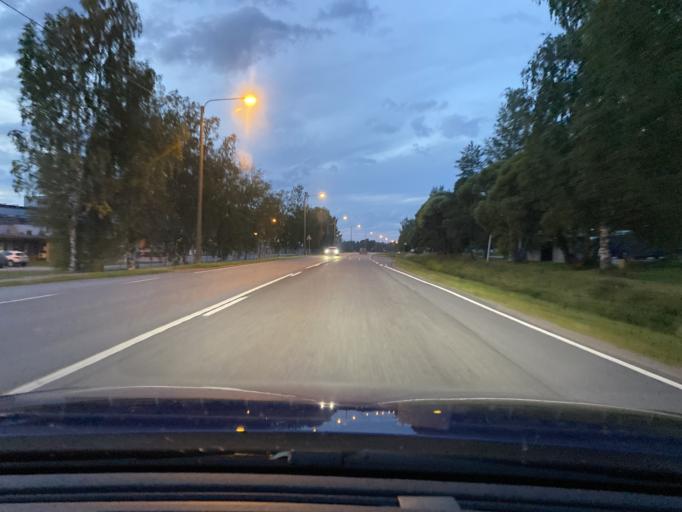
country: FI
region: Southern Ostrobothnia
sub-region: Suupohja
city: Kauhajoki
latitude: 62.4445
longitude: 22.2117
